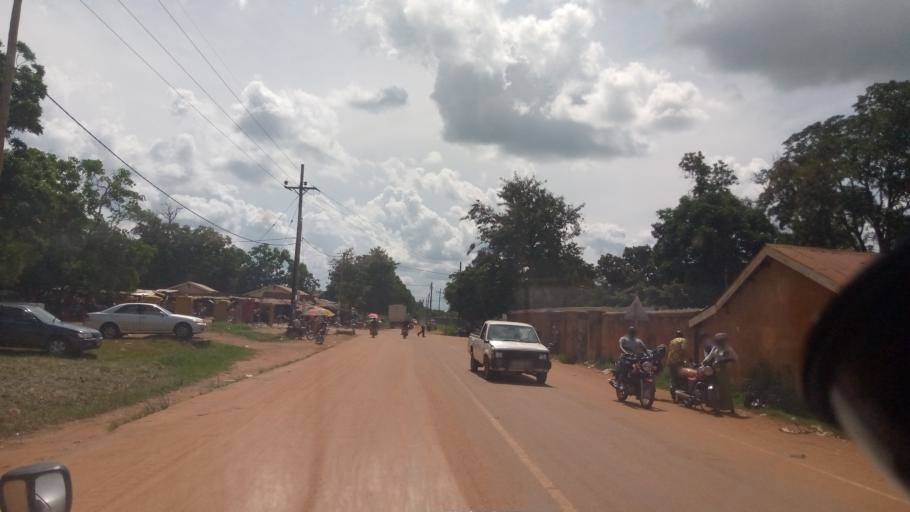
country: UG
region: Northern Region
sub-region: Lira District
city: Lira
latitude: 2.2500
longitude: 32.9028
